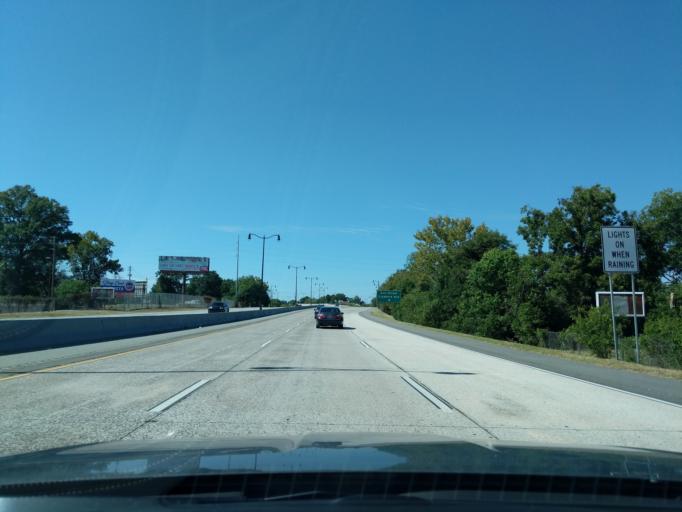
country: US
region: Georgia
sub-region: Richmond County
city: Augusta
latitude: 33.4806
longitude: -81.9899
